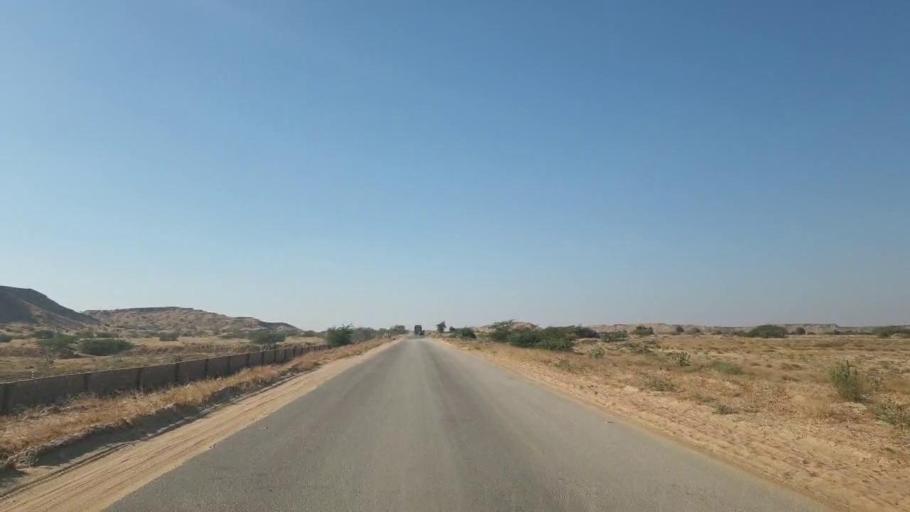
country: PK
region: Sindh
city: Gharo
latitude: 25.2172
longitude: 67.6262
